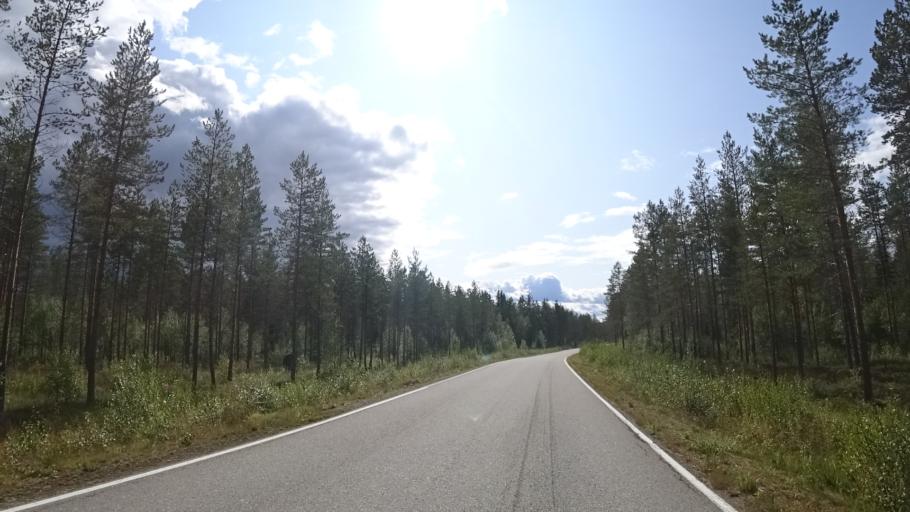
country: FI
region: North Karelia
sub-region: Joensuu
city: Ilomantsi
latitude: 62.4146
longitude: 31.0068
